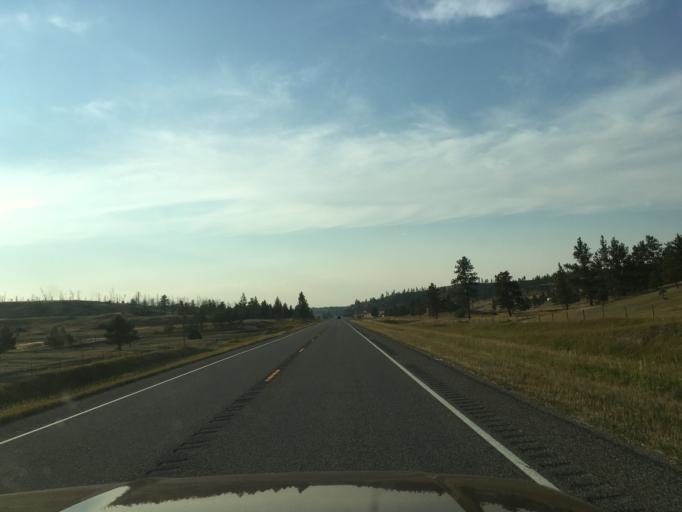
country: US
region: Montana
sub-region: Musselshell County
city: Roundup
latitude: 46.2856
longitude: -108.4796
